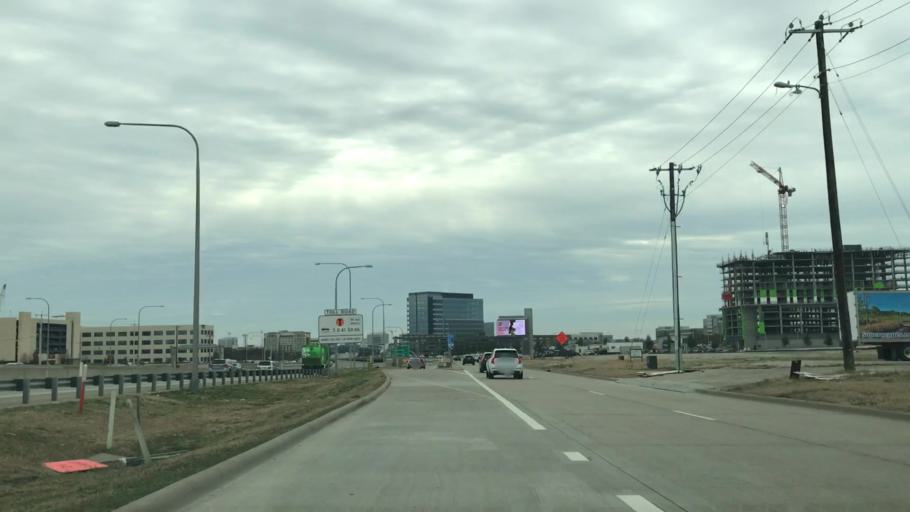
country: US
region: Texas
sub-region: Collin County
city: Frisco
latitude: 33.1122
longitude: -96.8239
